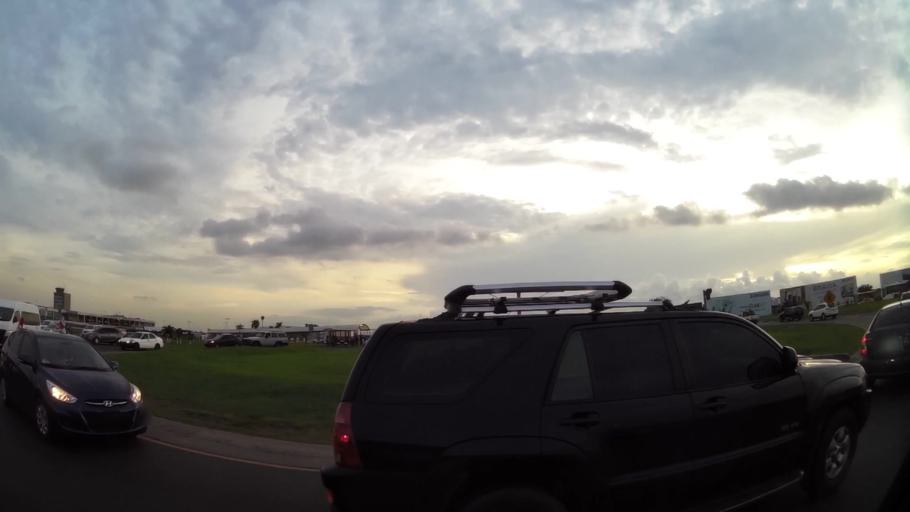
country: PA
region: Panama
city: Tocumen
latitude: 9.0715
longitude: -79.3881
